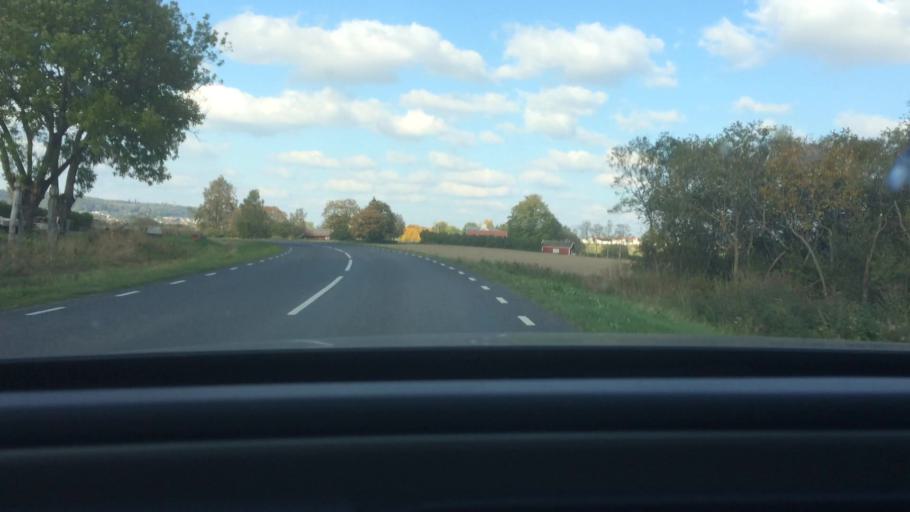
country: SE
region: Vaestra Goetaland
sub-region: Falkopings Kommun
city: Falkoeping
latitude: 58.1446
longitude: 13.5447
